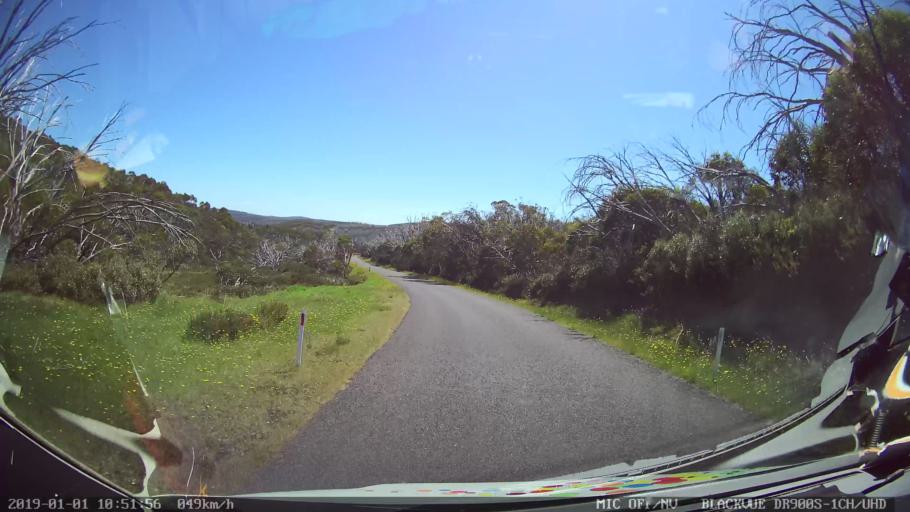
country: AU
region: New South Wales
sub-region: Snowy River
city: Jindabyne
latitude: -36.0189
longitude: 148.3762
